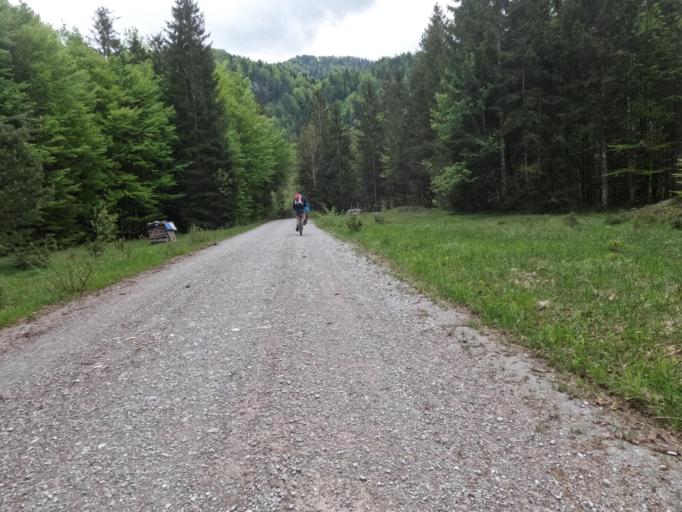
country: DE
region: Bavaria
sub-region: Upper Bavaria
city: Ruhpolding
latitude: 47.7097
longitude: 12.6603
